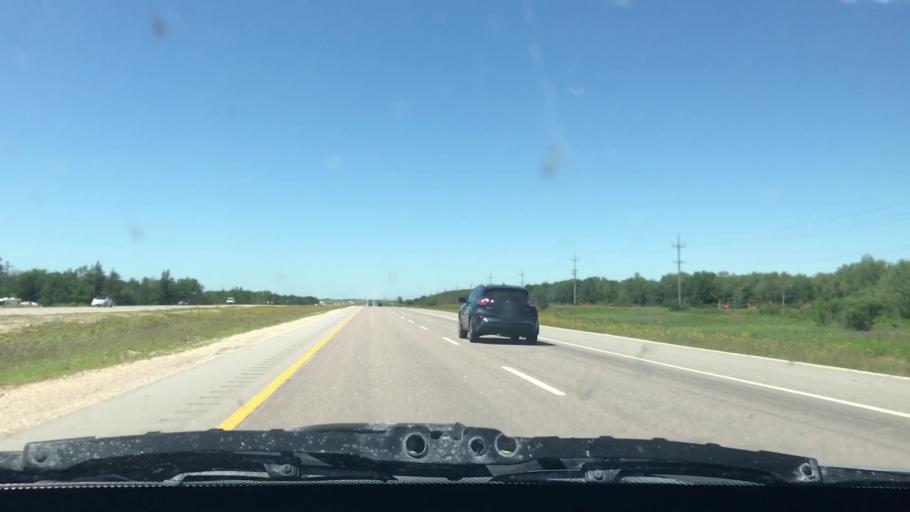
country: CA
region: Manitoba
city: Steinbach
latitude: 49.6810
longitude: -96.5955
